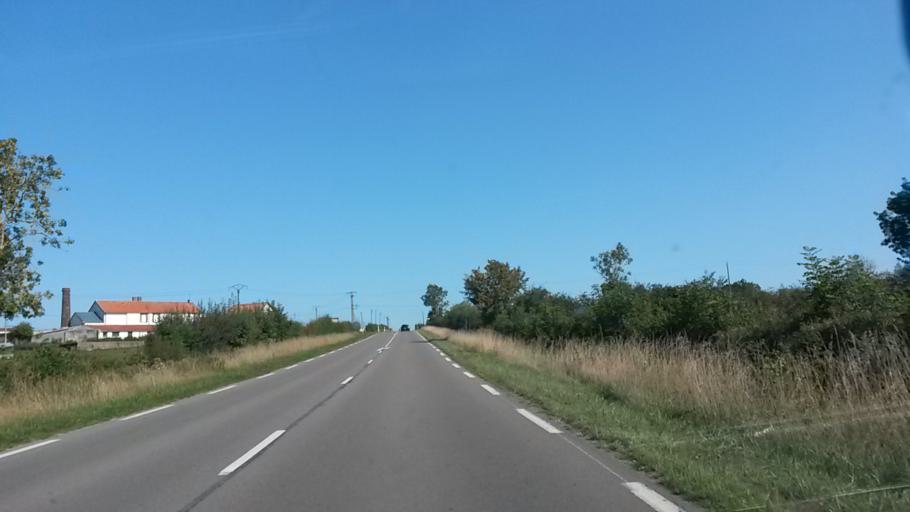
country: FR
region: Nord-Pas-de-Calais
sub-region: Departement du Nord
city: Avesnes-sur-Helpe
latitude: 50.0734
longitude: 3.9290
